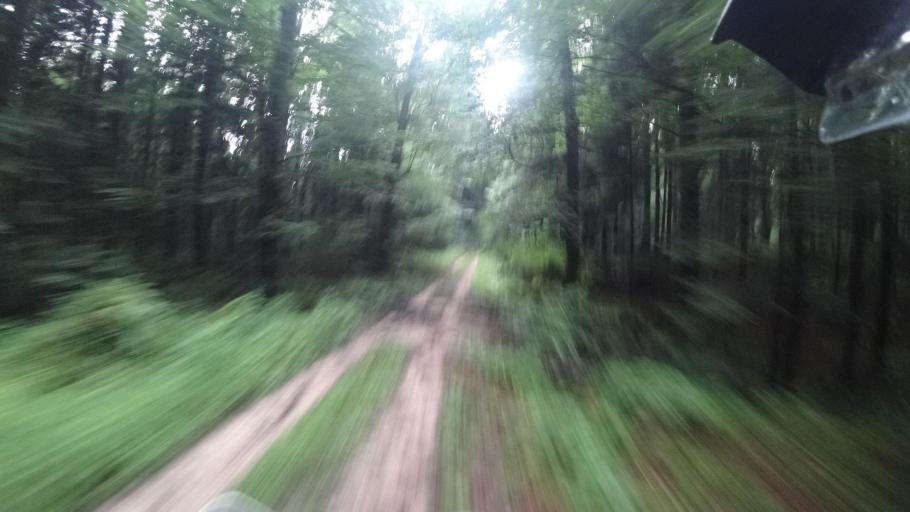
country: HR
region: Licko-Senjska
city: Jezerce
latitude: 44.8063
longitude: 15.6393
